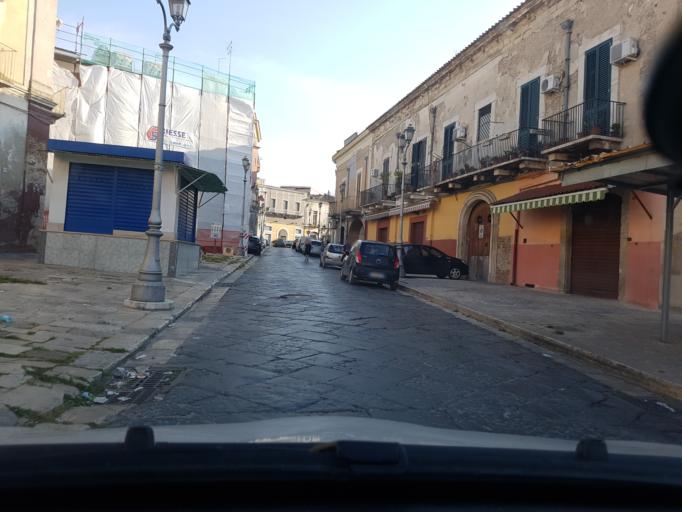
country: IT
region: Apulia
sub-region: Provincia di Foggia
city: Cerignola
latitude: 41.2665
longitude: 15.8948
